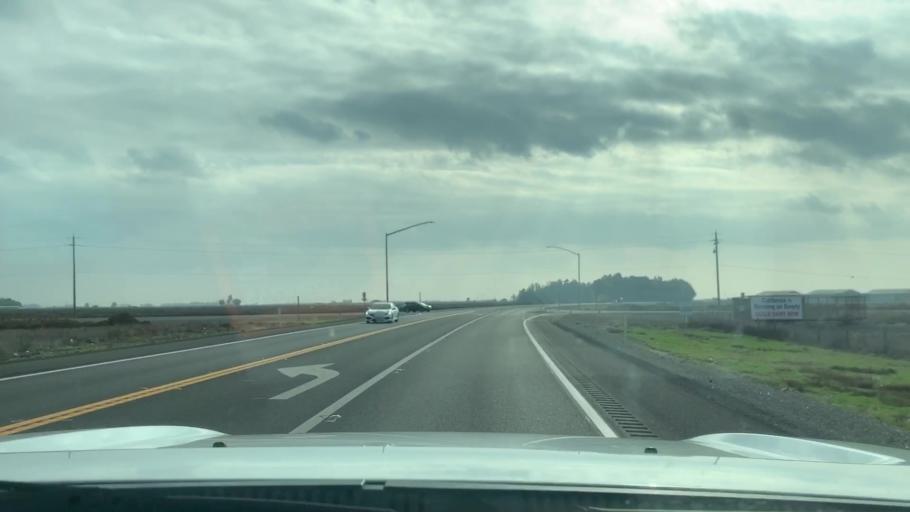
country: US
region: California
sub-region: Kings County
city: Lemoore
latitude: 36.2558
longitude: -119.8084
